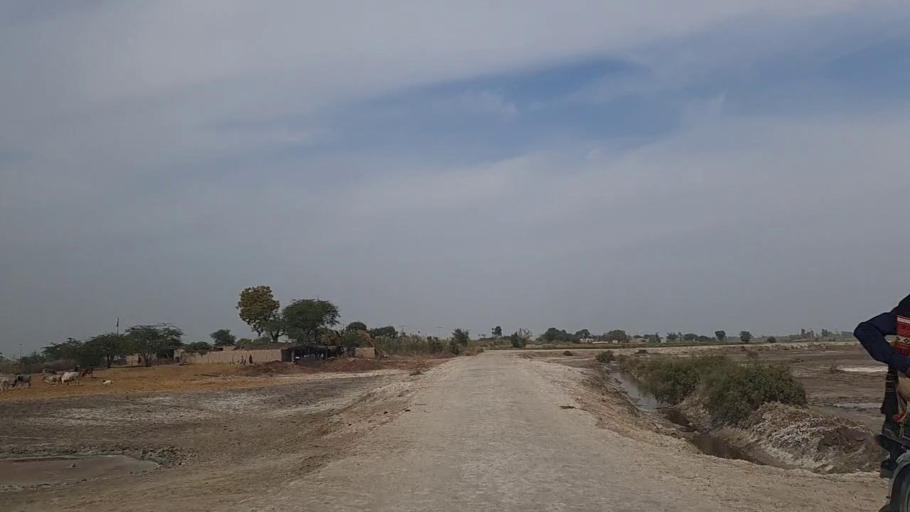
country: PK
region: Sindh
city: Daur
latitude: 26.4772
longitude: 68.4024
